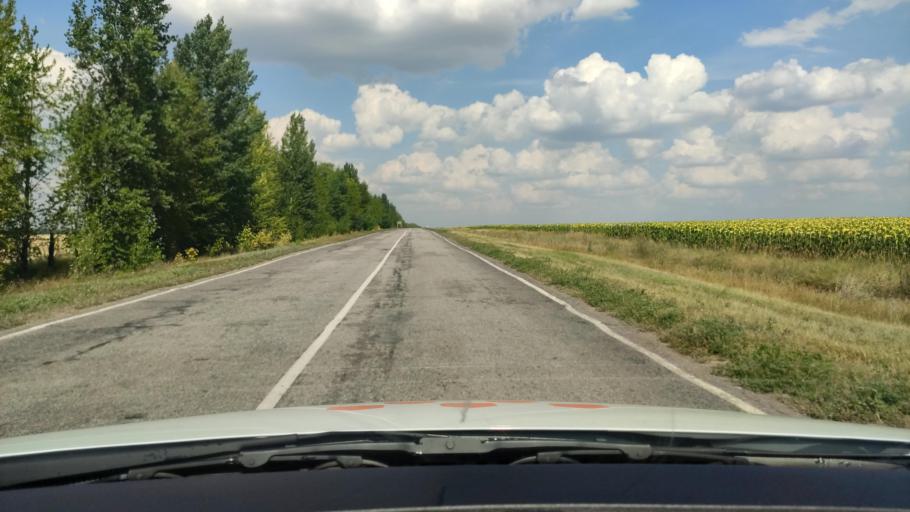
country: RU
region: Voronezj
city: Pereleshinskiy
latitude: 51.7479
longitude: 40.4103
